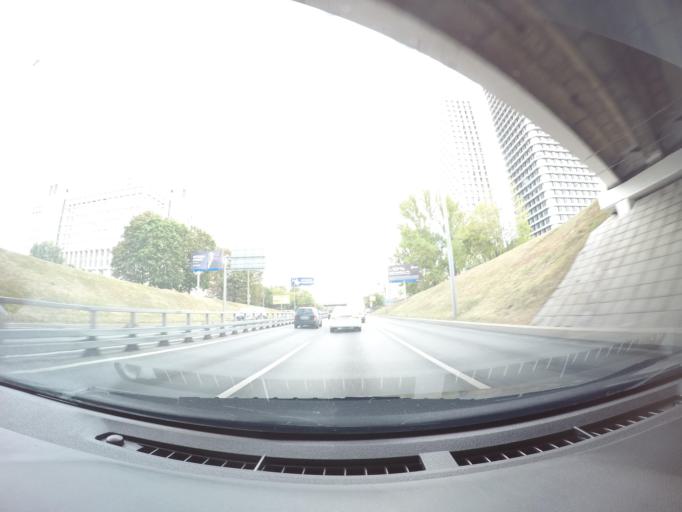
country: RU
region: Moscow
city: Mar'ina Roshcha
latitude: 55.8101
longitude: 37.5795
